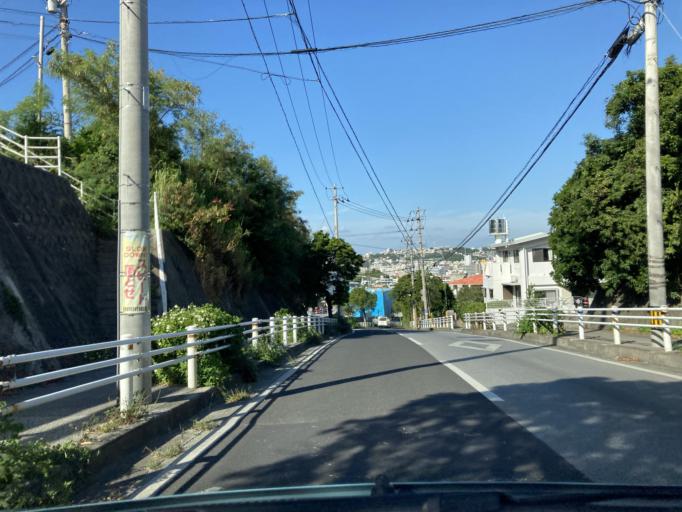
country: JP
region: Okinawa
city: Tomigusuku
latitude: 26.1784
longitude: 127.7062
